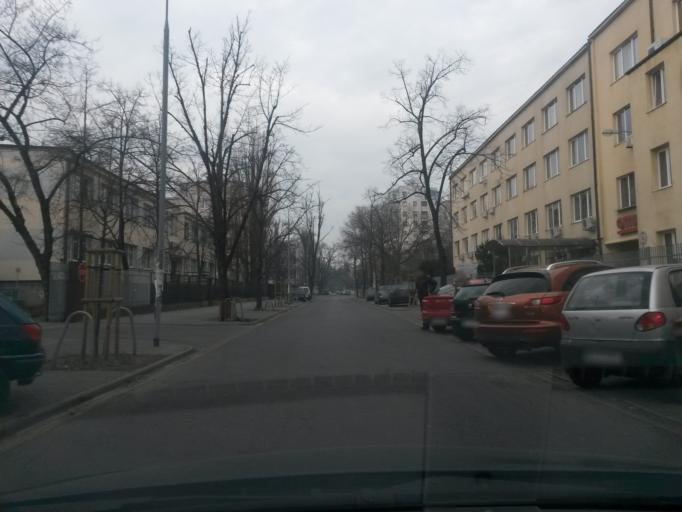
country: PL
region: Masovian Voivodeship
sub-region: Warszawa
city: Mokotow
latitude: 52.2055
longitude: 21.0377
